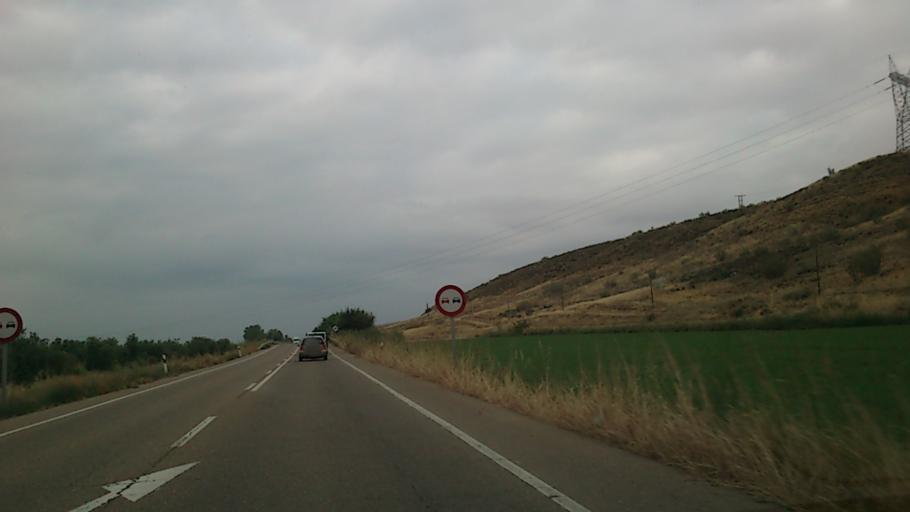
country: ES
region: Aragon
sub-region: Provincia de Zaragoza
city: San Mateo de Gallego
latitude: 41.8210
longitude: -0.8028
